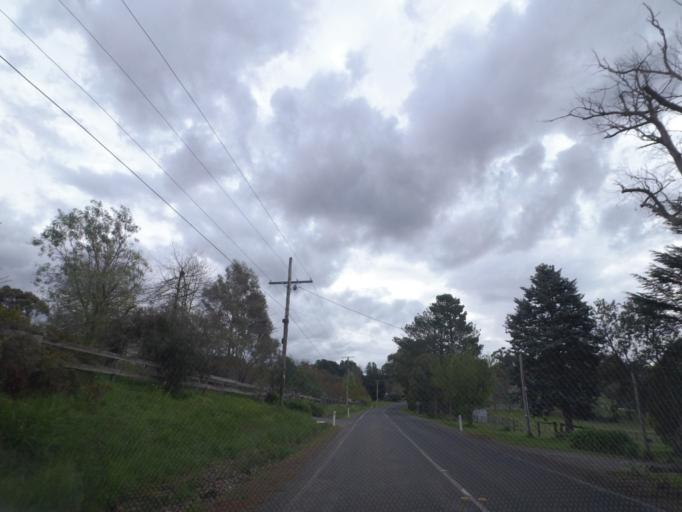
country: AU
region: Victoria
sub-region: Yarra Ranges
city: Mount Evelyn
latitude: -37.7701
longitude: 145.4236
